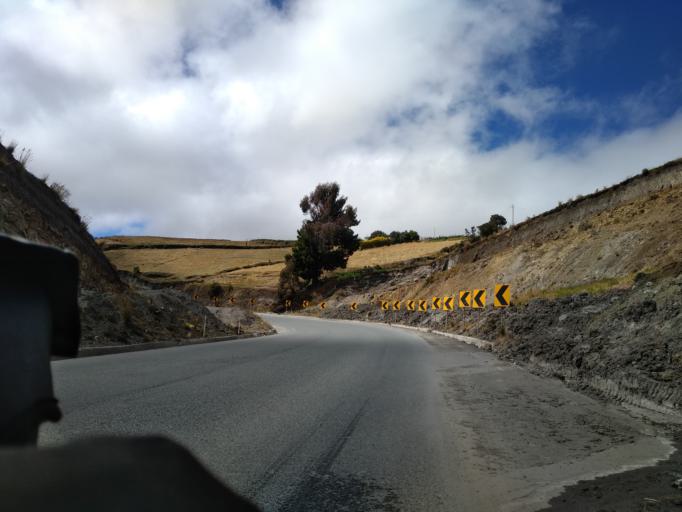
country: EC
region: Cotopaxi
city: Pujili
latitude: -0.9470
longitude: -78.9206
